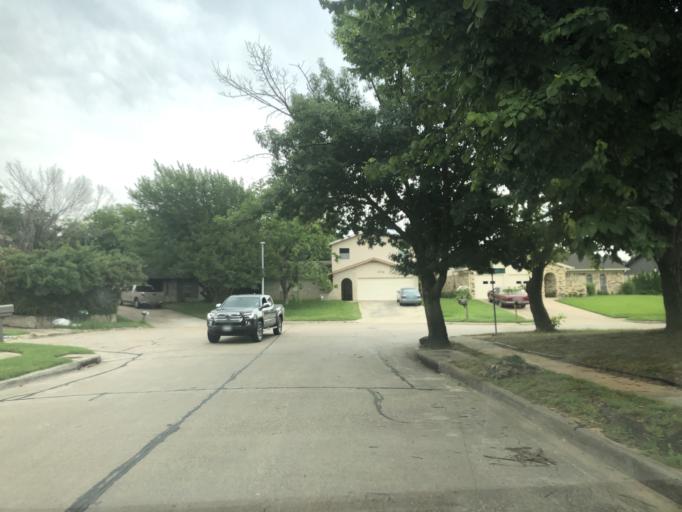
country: US
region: Texas
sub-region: Dallas County
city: Irving
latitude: 32.7853
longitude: -96.9636
